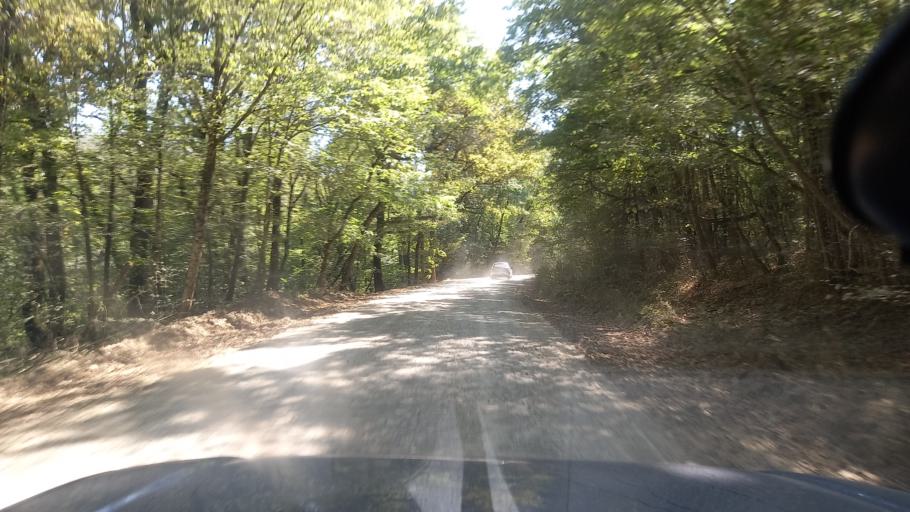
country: RU
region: Krasnodarskiy
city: Azovskaya
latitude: 44.6892
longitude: 38.6377
